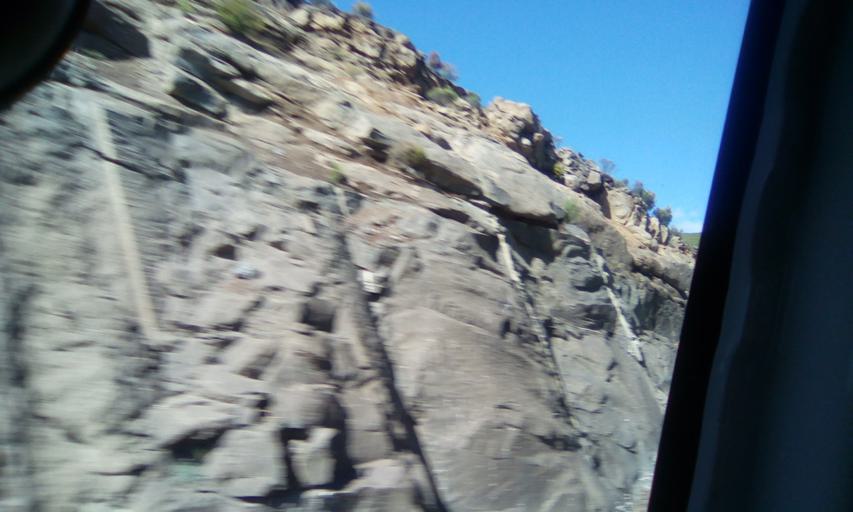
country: LS
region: Maseru
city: Nako
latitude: -29.9019
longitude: 28.1371
